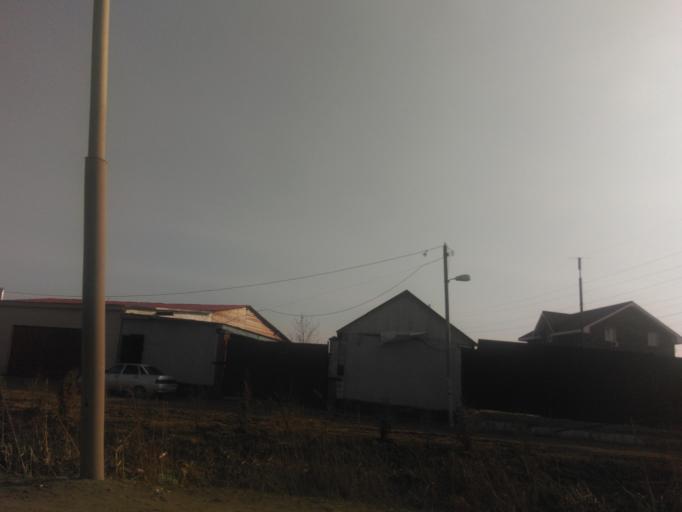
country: RU
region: Moskovskaya
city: Kokoshkino
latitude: 55.5888
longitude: 37.1188
